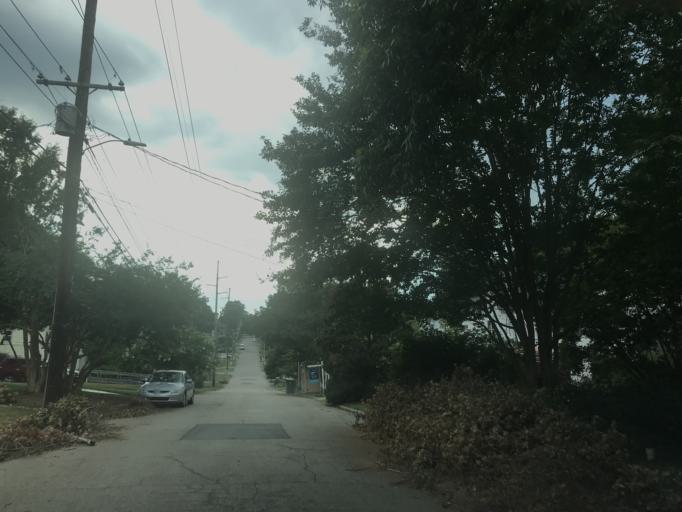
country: US
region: North Carolina
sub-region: Wake County
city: Raleigh
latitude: 35.8109
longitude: -78.6294
